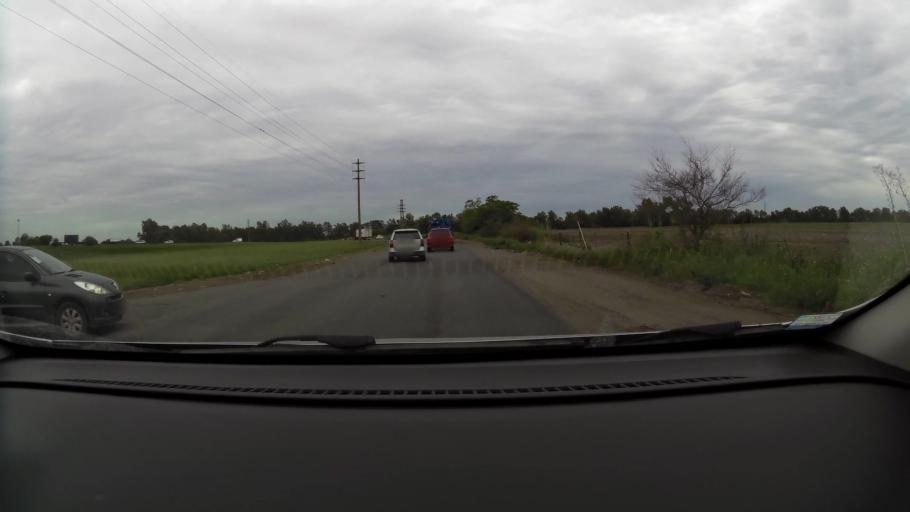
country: AR
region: Buenos Aires
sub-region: Partido de Zarate
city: Zarate
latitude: -34.1125
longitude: -59.1143
